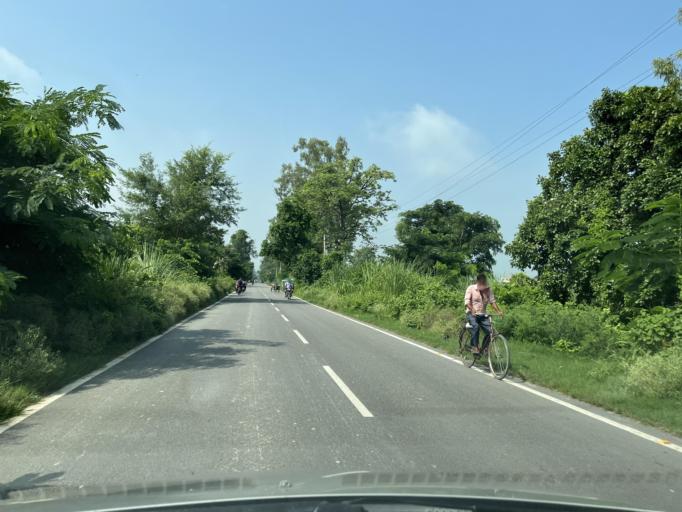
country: IN
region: Uttarakhand
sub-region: Udham Singh Nagar
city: Bazpur
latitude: 29.1855
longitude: 79.1845
